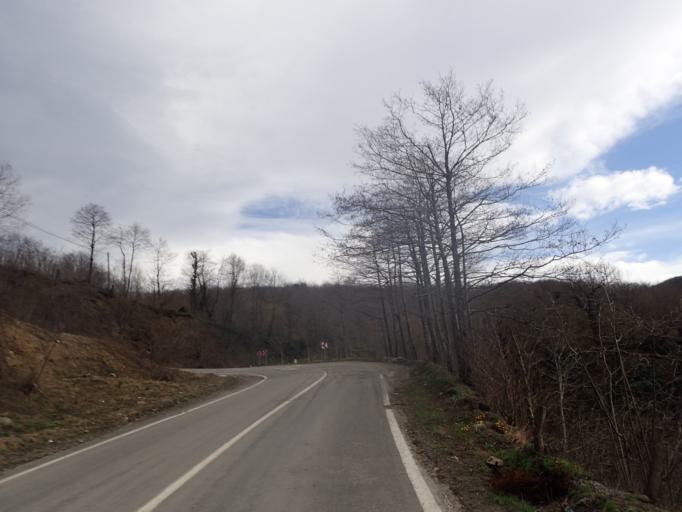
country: TR
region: Ordu
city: Camas
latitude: 40.8877
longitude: 37.5299
